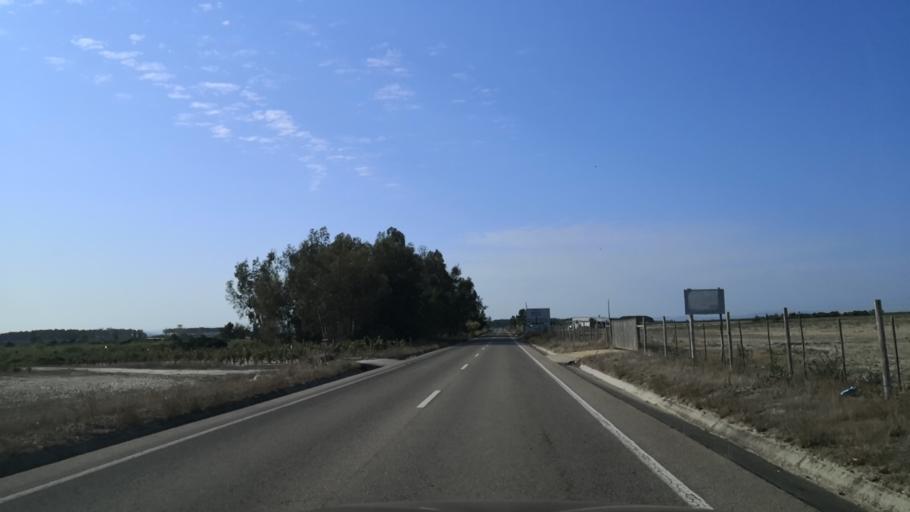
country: PT
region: Santarem
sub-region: Almeirim
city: Fazendas de Almeirim
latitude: 39.1481
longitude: -8.6165
